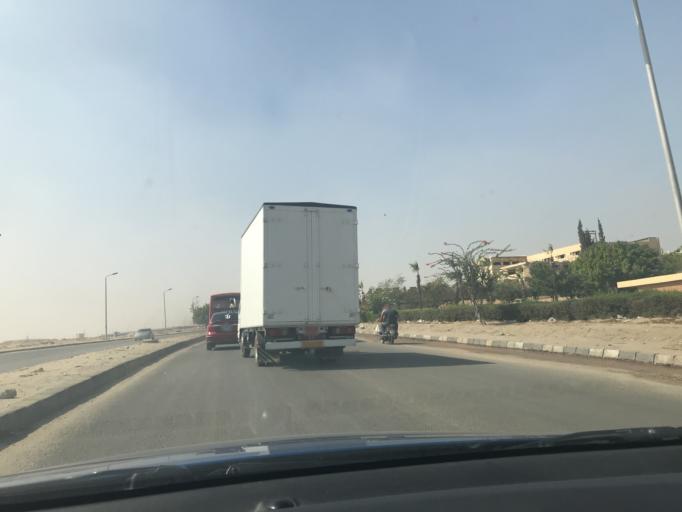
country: EG
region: Eastern Province
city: Bilbays
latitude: 30.2555
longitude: 31.7575
